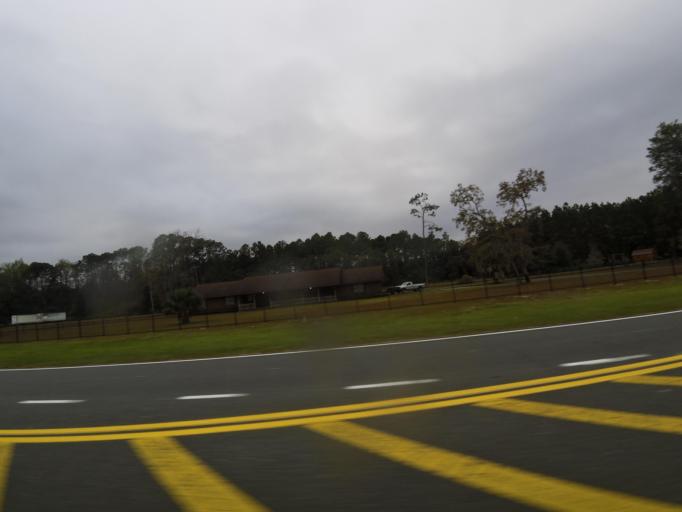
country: US
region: Georgia
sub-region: Charlton County
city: Folkston
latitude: 30.8244
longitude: -82.0100
